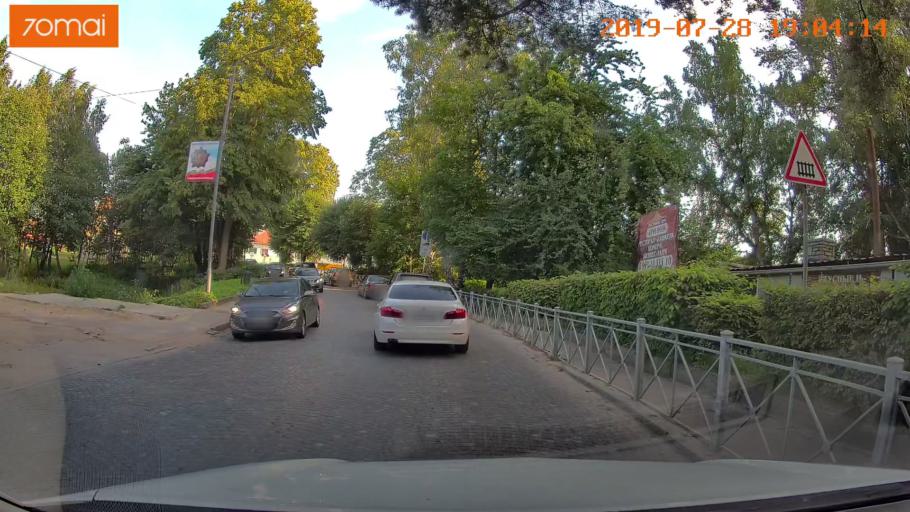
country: RU
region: Kaliningrad
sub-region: Gorod Svetlogorsk
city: Svetlogorsk
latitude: 54.9342
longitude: 20.1613
